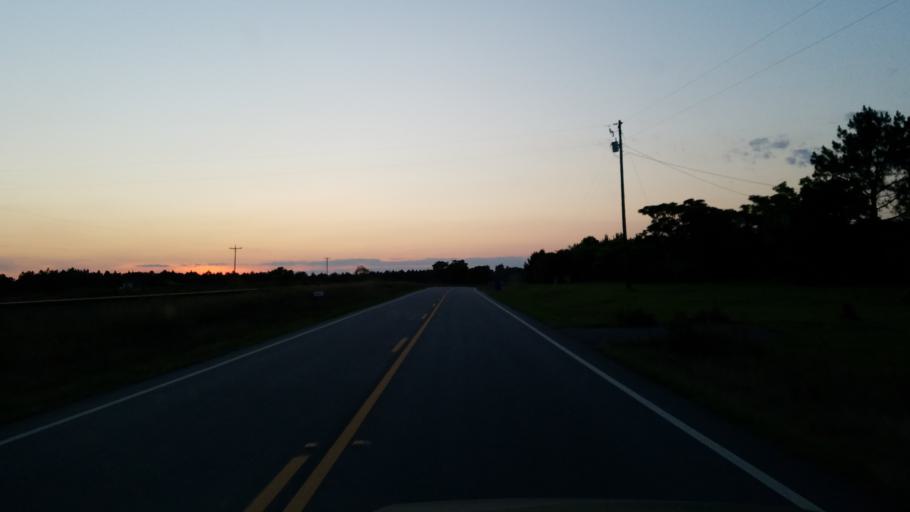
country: US
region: Georgia
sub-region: Turner County
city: Ashburn
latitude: 31.6134
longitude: -83.6024
